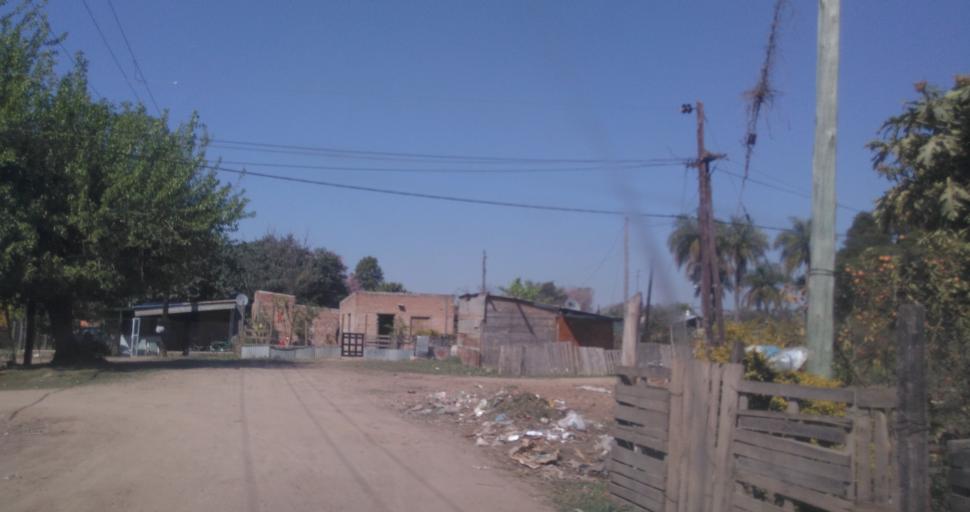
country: AR
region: Chaco
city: Fontana
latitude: -27.4232
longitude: -59.0148
